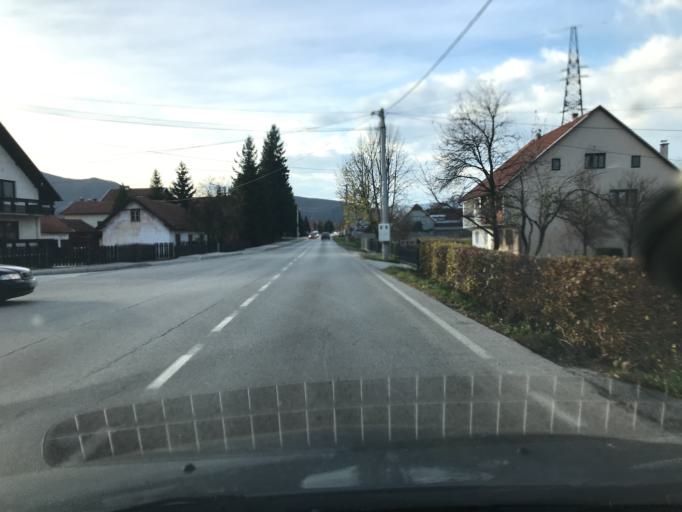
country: BA
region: Federation of Bosnia and Herzegovina
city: Vitez
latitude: 44.1627
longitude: 17.7788
